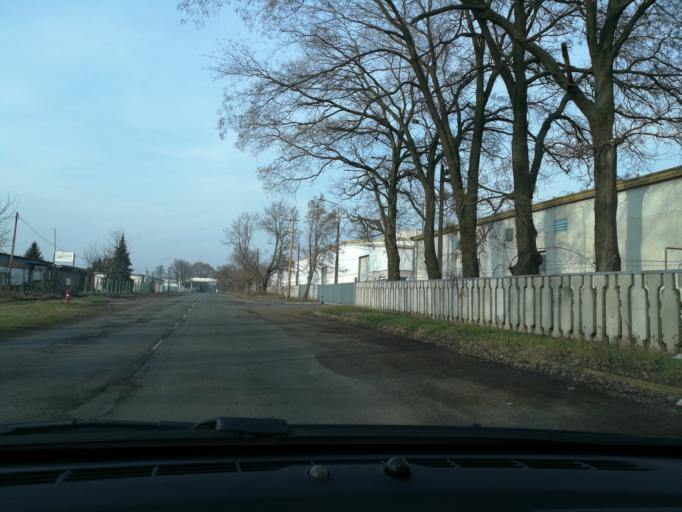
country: HU
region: Szabolcs-Szatmar-Bereg
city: Nyiregyhaza
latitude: 47.9469
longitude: 21.7022
